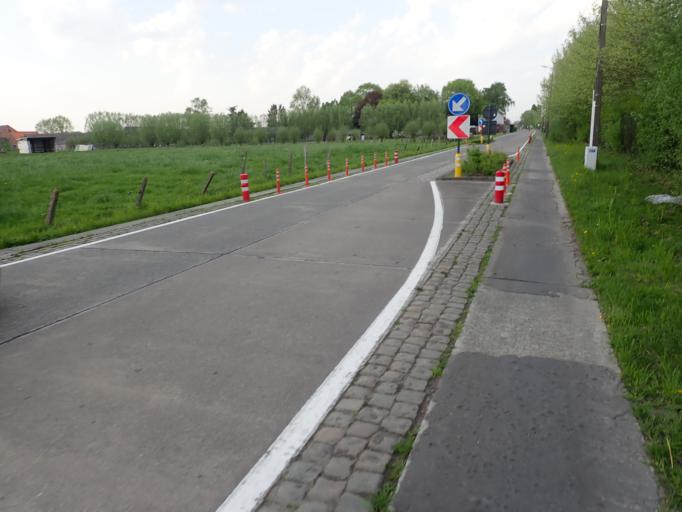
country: BE
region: Flanders
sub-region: Provincie Vlaams-Brabant
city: Londerzeel
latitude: 51.0309
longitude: 4.3216
